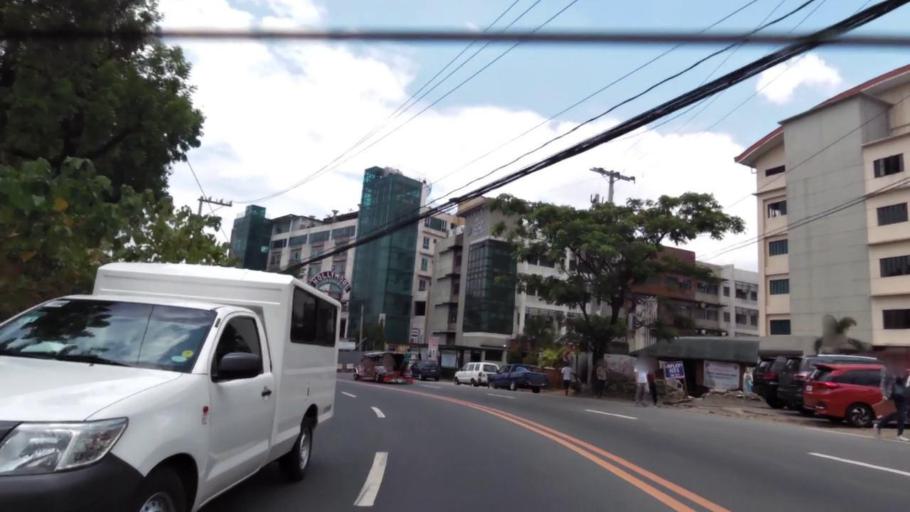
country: PH
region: Calabarzon
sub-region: Province of Rizal
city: Antipolo
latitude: 14.6188
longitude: 121.1522
